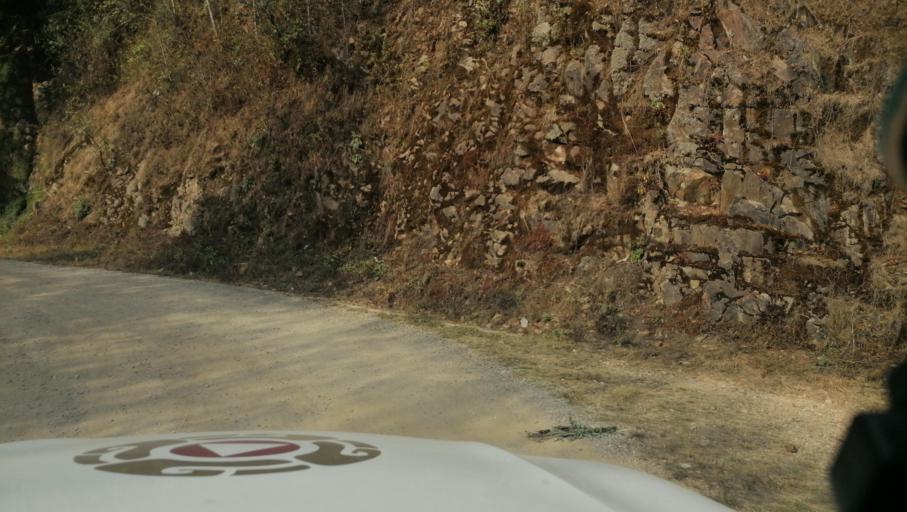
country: GT
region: San Marcos
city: Tacana
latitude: 15.2279
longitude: -92.1927
